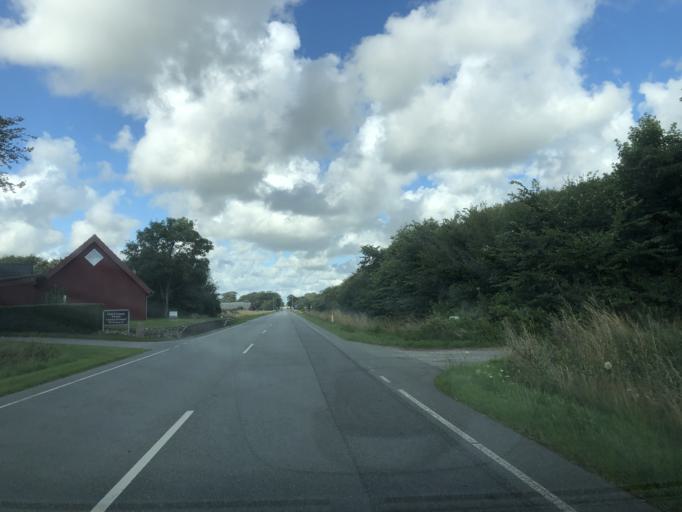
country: DK
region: Central Jutland
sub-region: Lemvig Kommune
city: Lemvig
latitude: 56.4977
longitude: 8.2523
